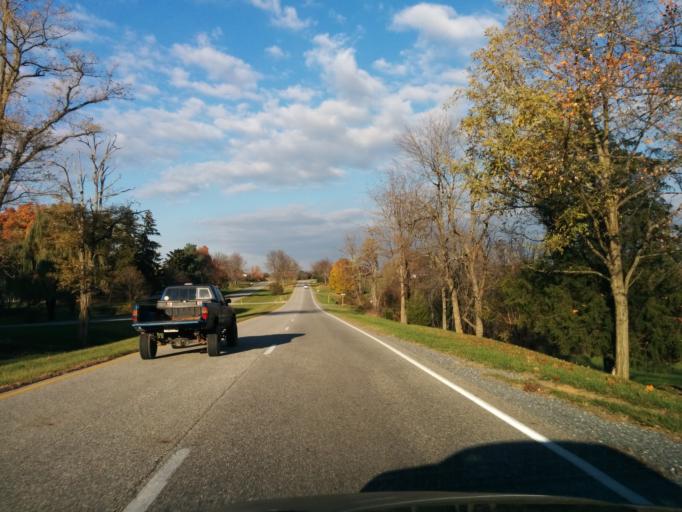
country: US
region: Virginia
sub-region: Rockbridge County
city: East Lexington
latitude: 37.8612
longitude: -79.3182
